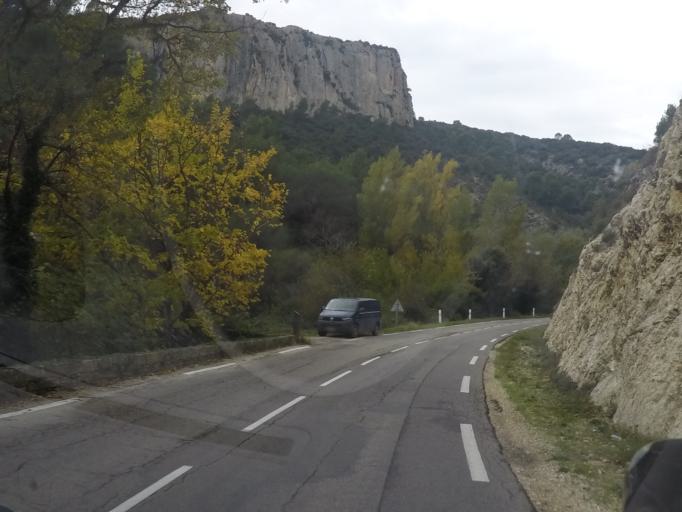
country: FR
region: Provence-Alpes-Cote d'Azur
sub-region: Departement du Vaucluse
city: Lourmarin
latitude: 43.7751
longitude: 5.3514
